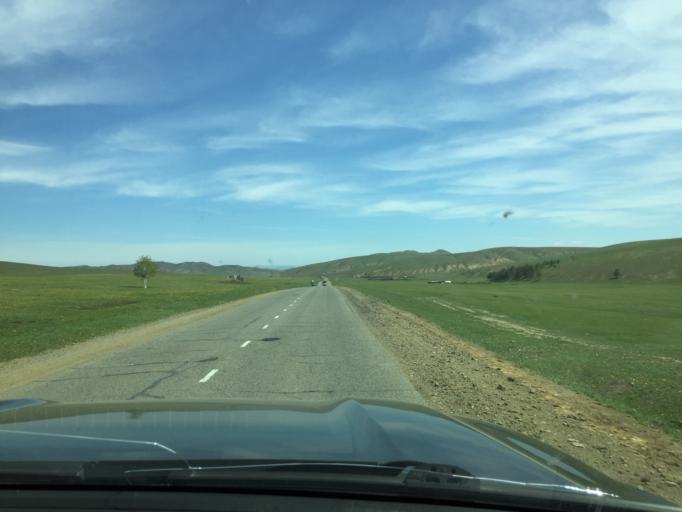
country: MN
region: Central Aimak
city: Javhlant
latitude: 48.6579
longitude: 106.1174
